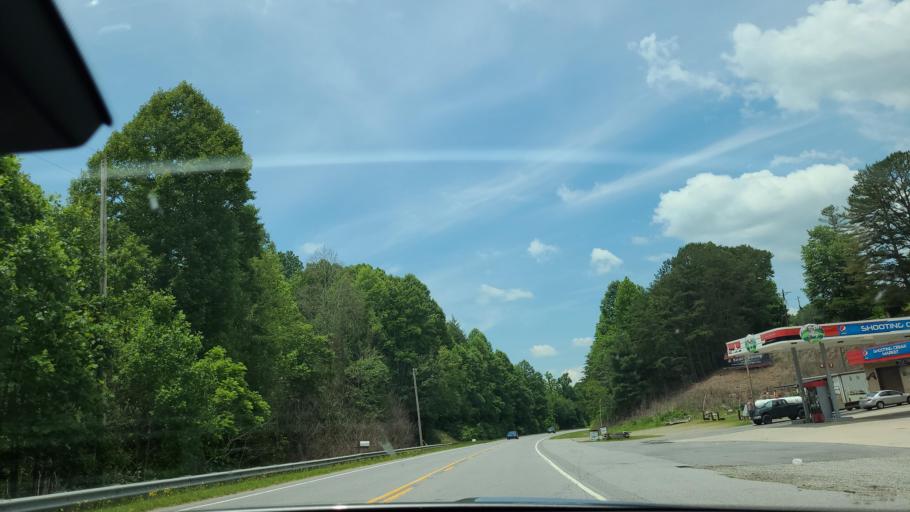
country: US
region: Georgia
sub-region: Towns County
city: Hiawassee
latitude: 35.0224
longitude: -83.6941
